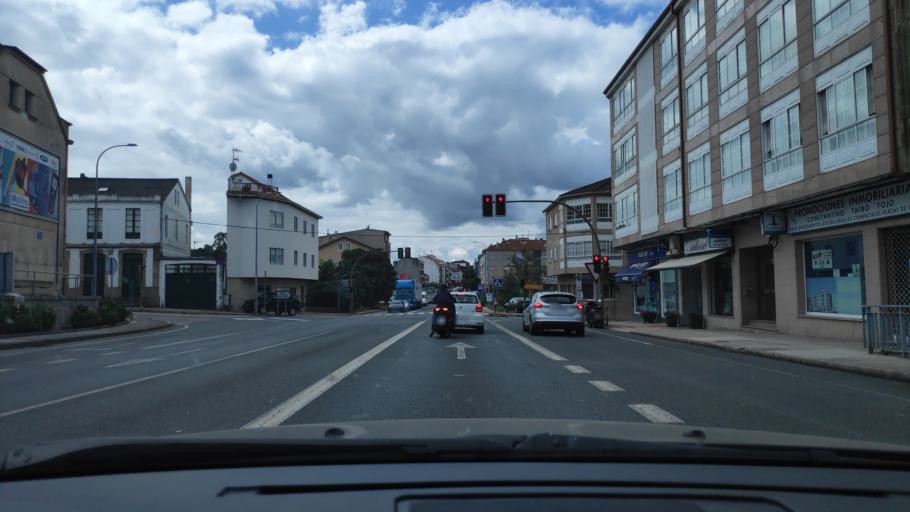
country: ES
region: Galicia
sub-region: Provincia da Coruna
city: Padron
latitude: 42.7198
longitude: -8.6510
